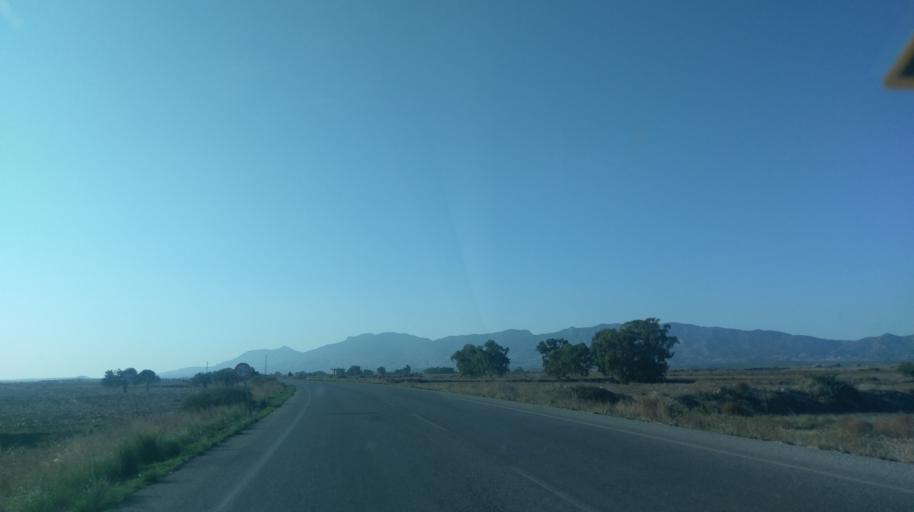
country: CY
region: Ammochostos
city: Lefkonoiko
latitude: 35.2577
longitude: 33.6801
